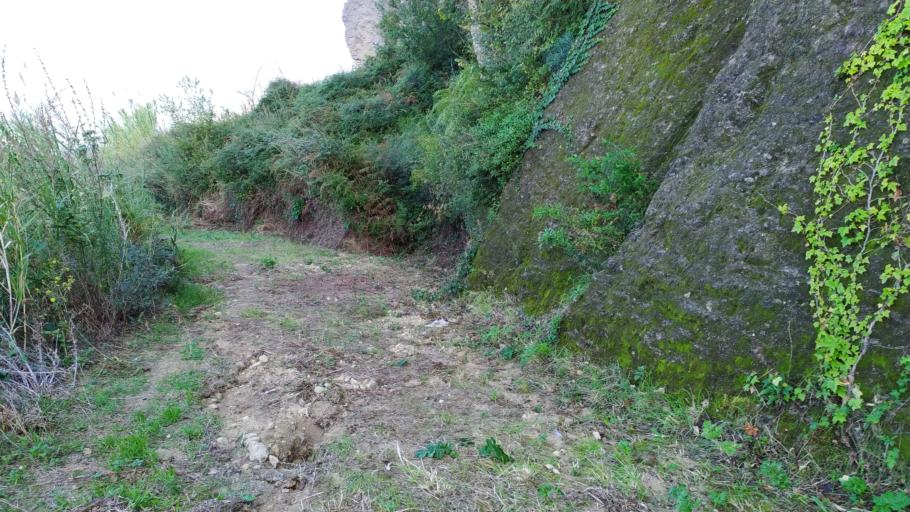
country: IT
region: Sicily
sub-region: Messina
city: Rometta
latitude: 38.1744
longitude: 15.4167
